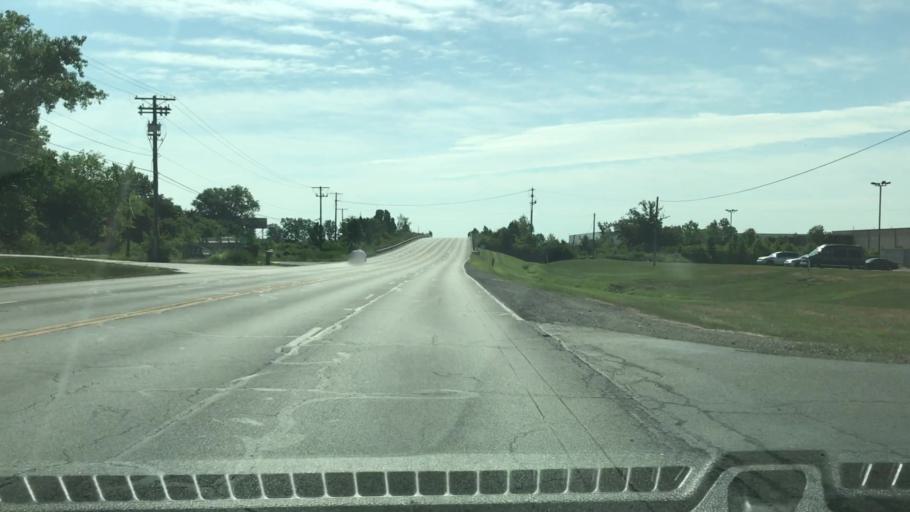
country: US
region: Ohio
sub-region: Franklin County
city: Lincoln Village
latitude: 39.9733
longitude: -83.1348
